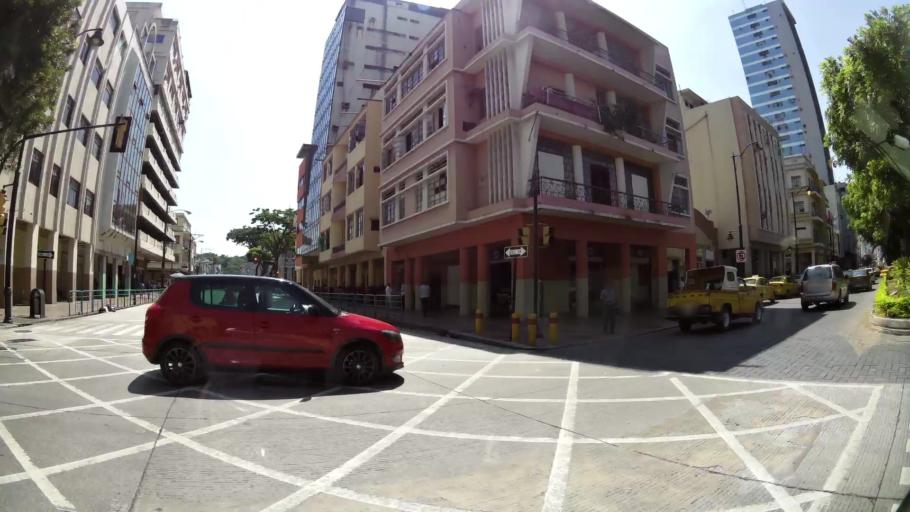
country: EC
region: Guayas
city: Guayaquil
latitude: -2.1888
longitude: -79.8882
